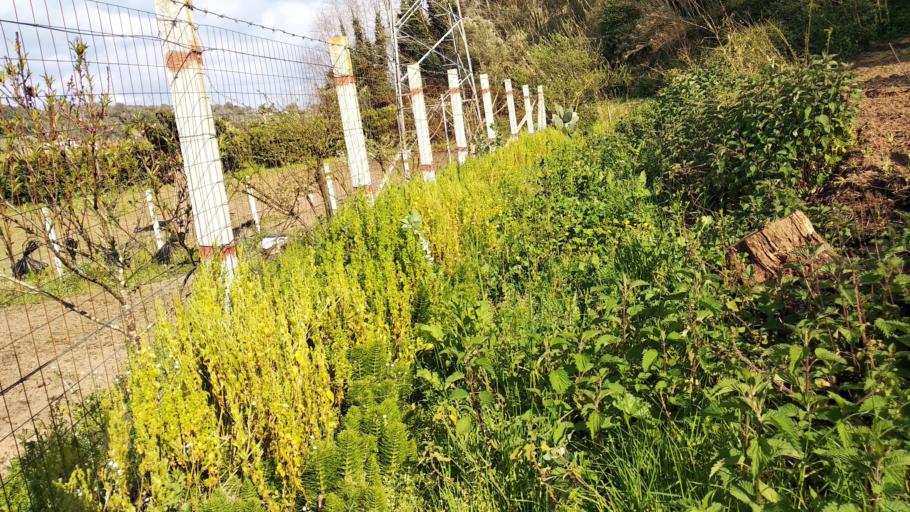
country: IT
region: Calabria
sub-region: Provincia di Reggio Calabria
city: Rizziconi
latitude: 38.4289
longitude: 15.9595
